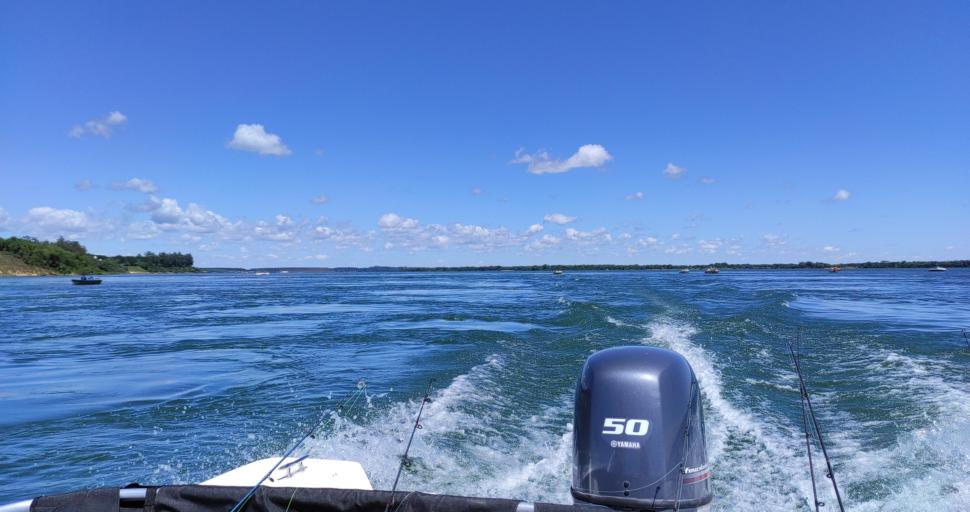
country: AR
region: Corrientes
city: Ituzaingo
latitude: -27.5883
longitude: -56.7933
